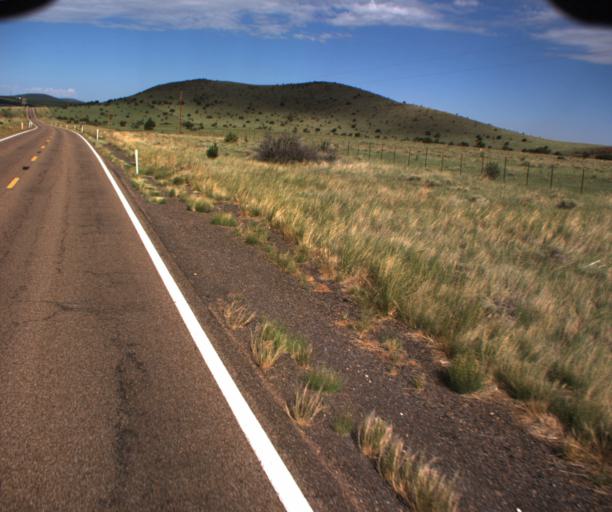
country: US
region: Arizona
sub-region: Navajo County
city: Pinetop-Lakeside
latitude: 34.2702
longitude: -109.6362
